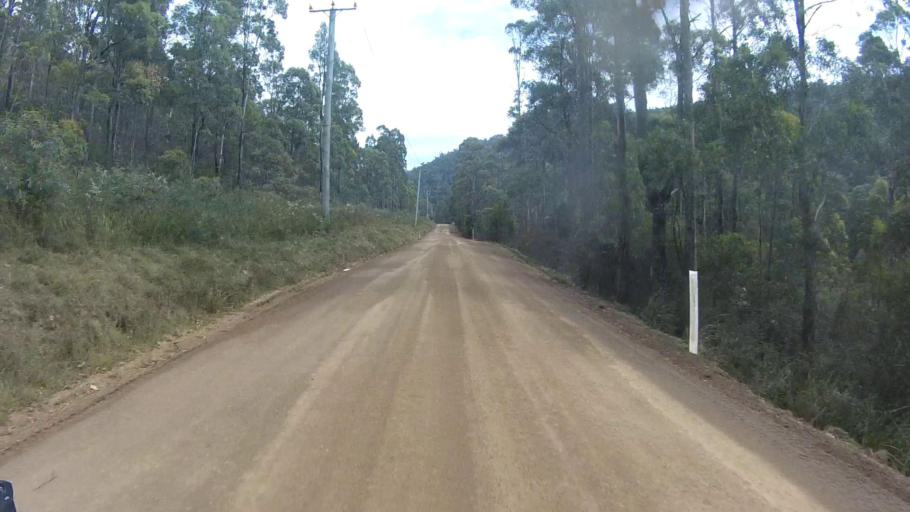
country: AU
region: Tasmania
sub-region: Sorell
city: Sorell
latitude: -42.7459
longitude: 147.7813
